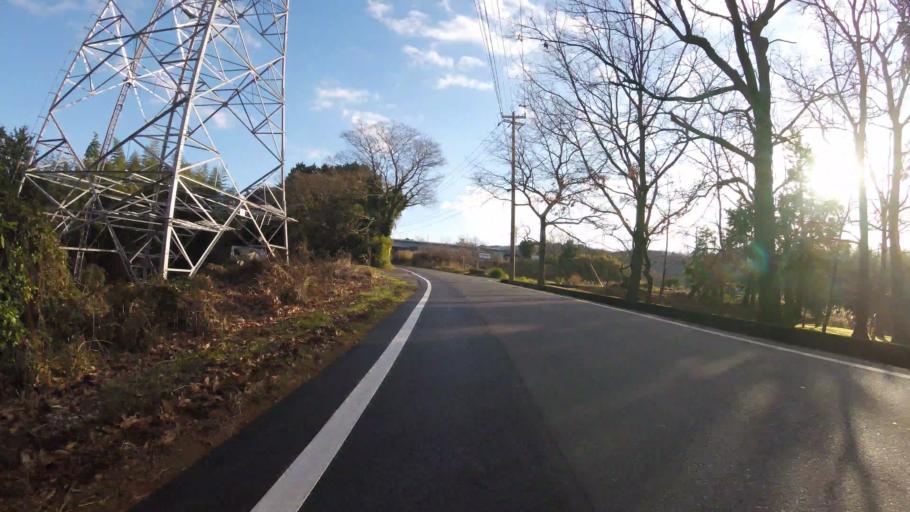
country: JP
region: Shizuoka
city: Mishima
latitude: 35.1067
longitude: 138.9810
